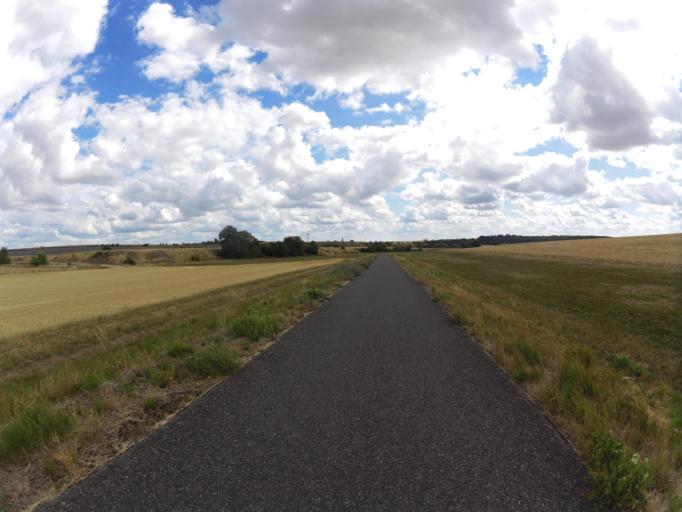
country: DE
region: Bavaria
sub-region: Regierungsbezirk Unterfranken
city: Aub
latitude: 49.5598
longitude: 10.0531
